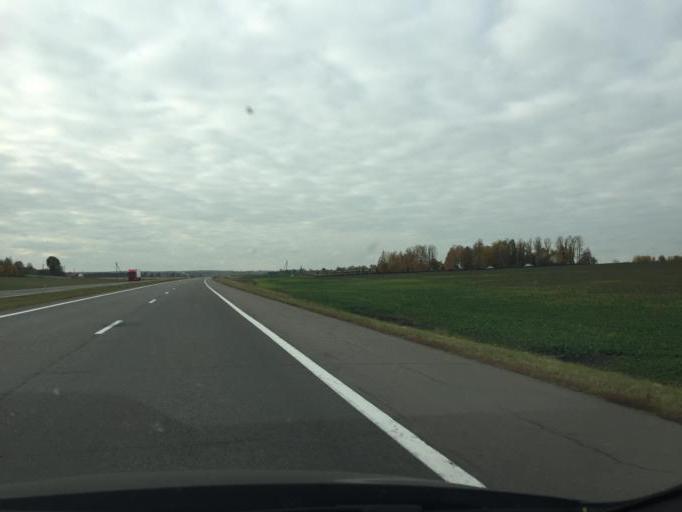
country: BY
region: Minsk
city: Stan'kava
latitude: 53.6778
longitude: 27.2649
